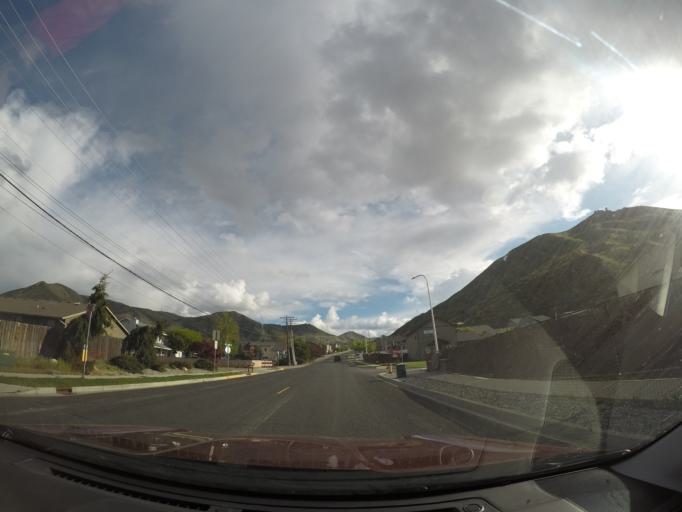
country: US
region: Washington
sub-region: Chelan County
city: South Wenatchee
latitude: 47.3932
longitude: -120.3084
